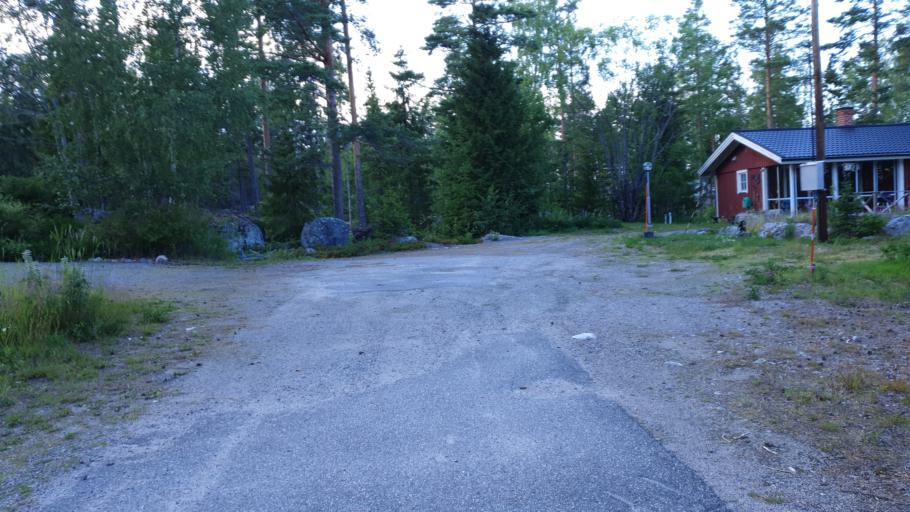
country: SE
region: Gaevleborg
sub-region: Soderhamns Kommun
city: Marielund
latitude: 61.4224
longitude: 17.1543
